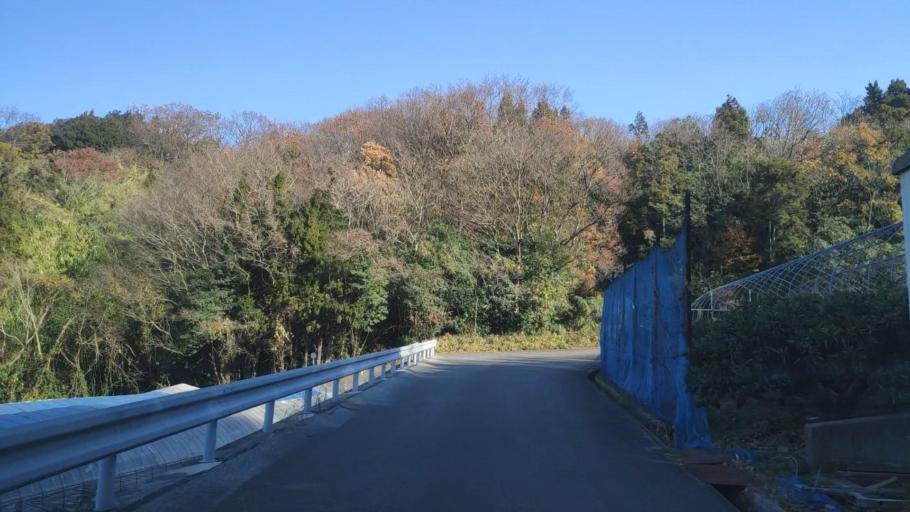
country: JP
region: Hiroshima
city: Innoshima
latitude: 34.2156
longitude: 133.1260
